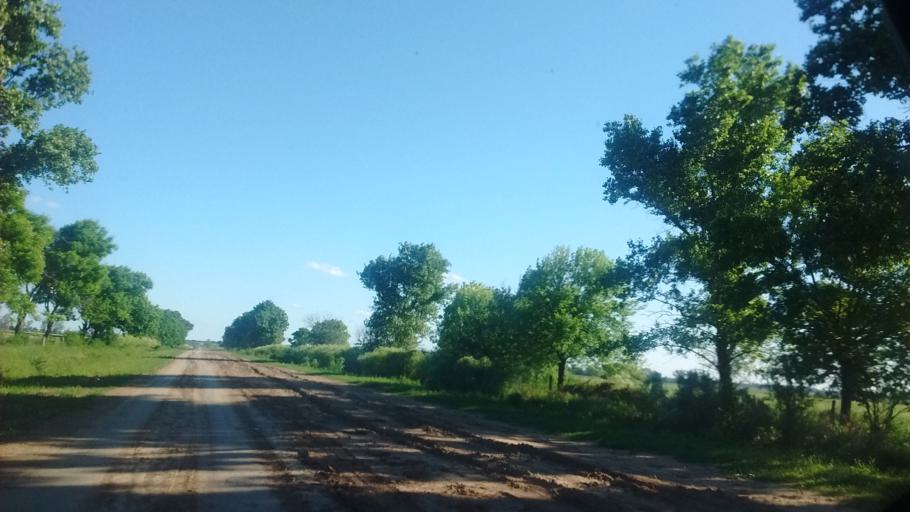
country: AR
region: Santa Fe
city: Funes
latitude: -32.8757
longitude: -60.7984
